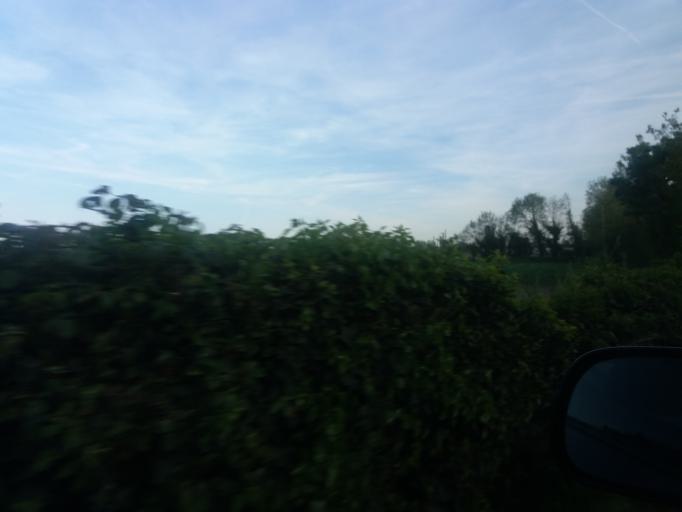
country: IE
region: Leinster
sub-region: Fingal County
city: Swords
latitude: 53.4861
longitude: -6.2202
